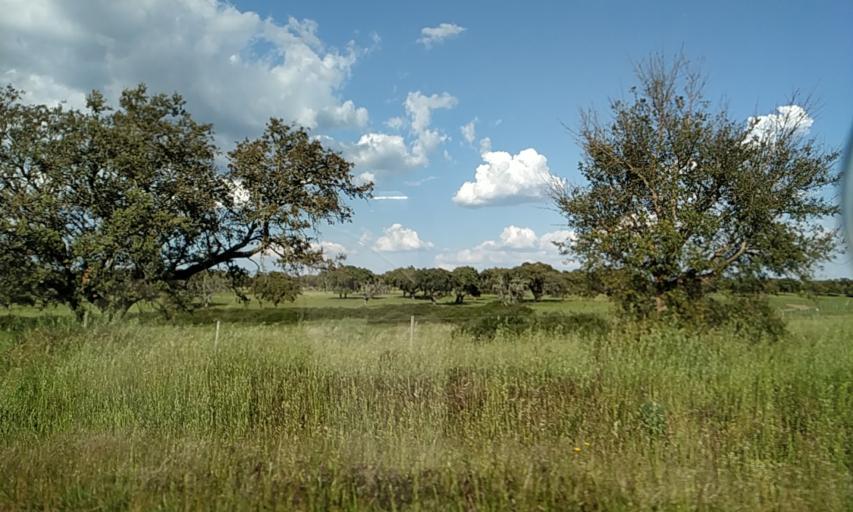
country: PT
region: Portalegre
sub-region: Portalegre
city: Urra
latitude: 39.1651
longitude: -7.4539
